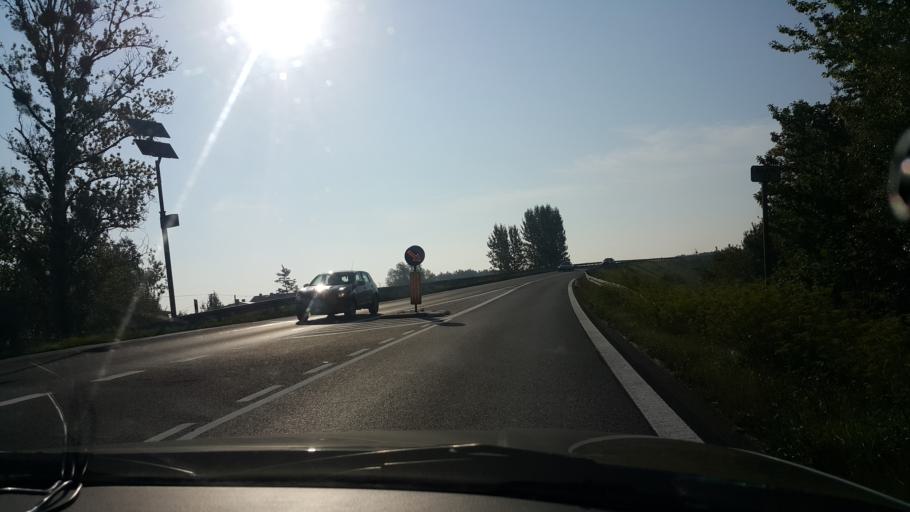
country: PL
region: Masovian Voivodeship
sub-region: Powiat radomski
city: Jastrzebia
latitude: 51.4131
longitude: 21.2337
